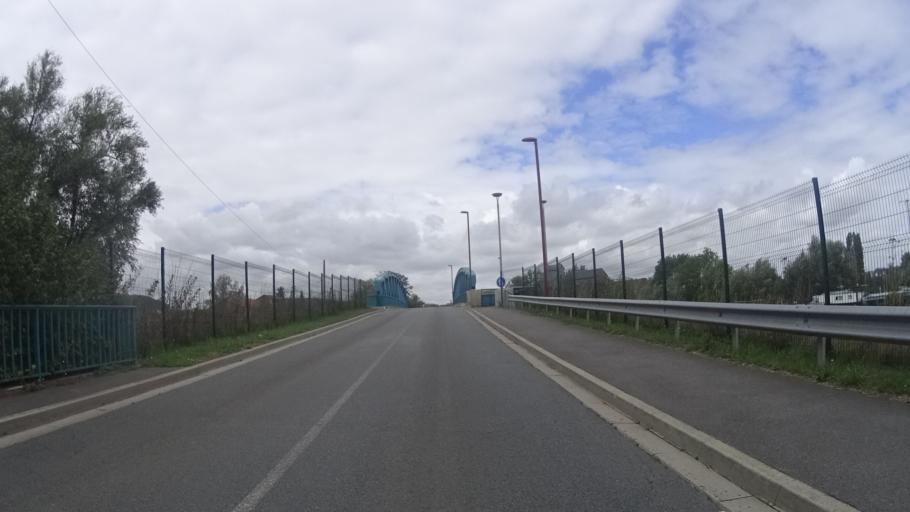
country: FR
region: Picardie
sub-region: Departement de l'Oise
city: Noyon
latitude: 49.5612
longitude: 2.9923
